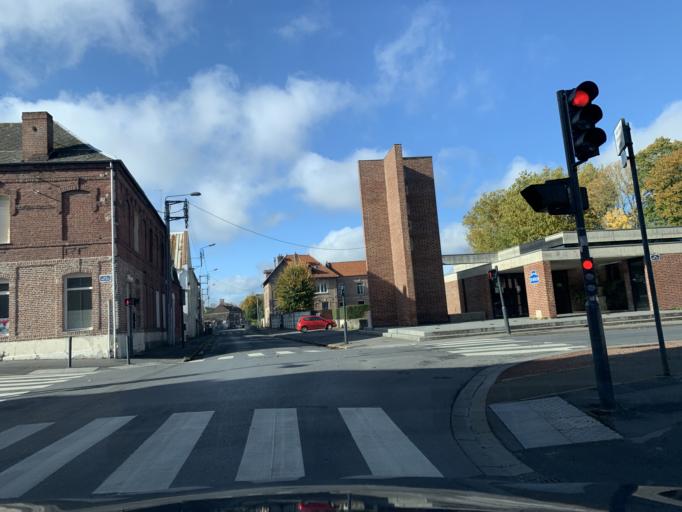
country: FR
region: Nord-Pas-de-Calais
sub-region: Departement du Nord
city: Neuville-Saint-Remy
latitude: 50.1856
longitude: 3.2434
